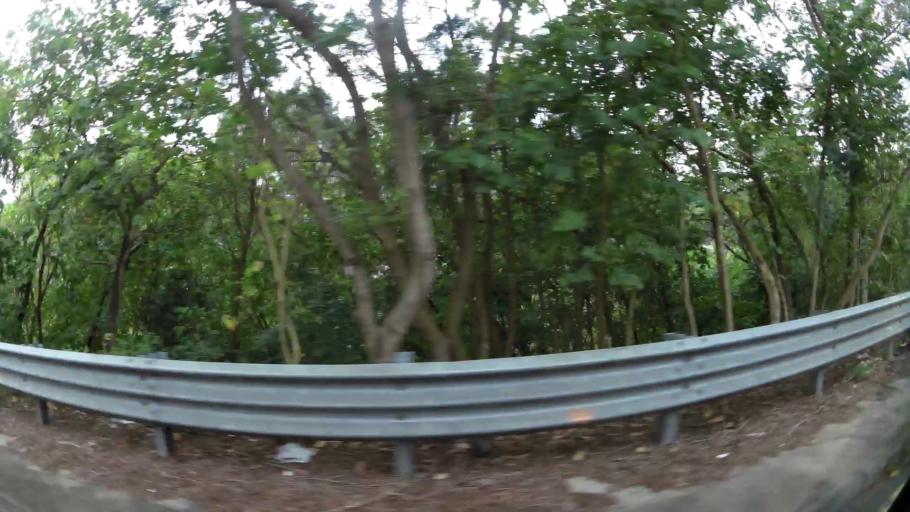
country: HK
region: Sha Tin
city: Sha Tin
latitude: 22.3919
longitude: 114.1966
